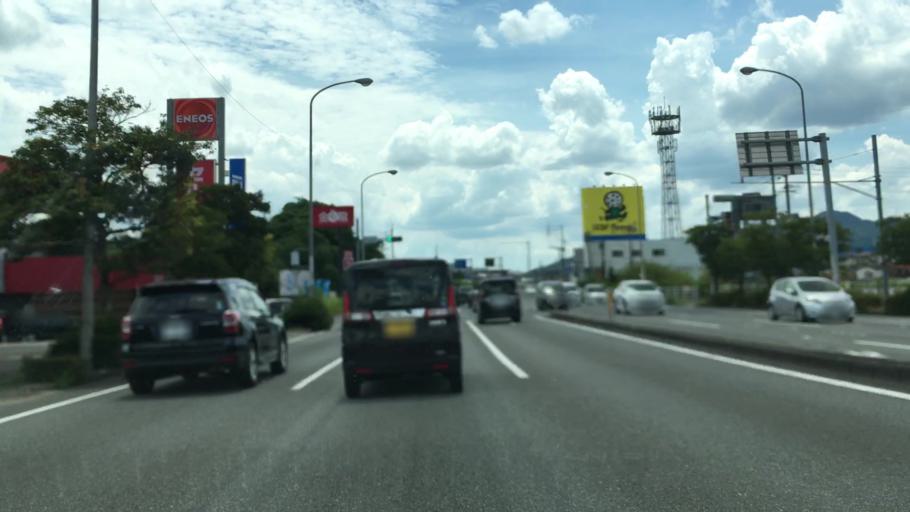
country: JP
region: Fukuoka
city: Chikushino-shi
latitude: 33.4935
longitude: 130.5355
